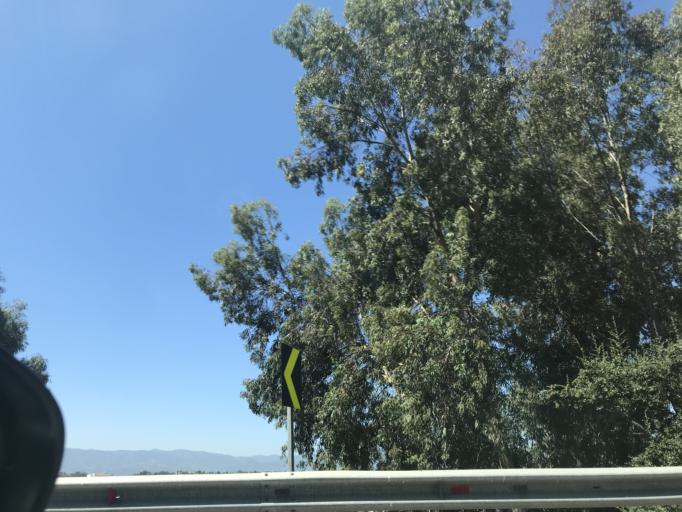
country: TR
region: Aydin
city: Aydin
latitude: 37.8175
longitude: 27.8446
